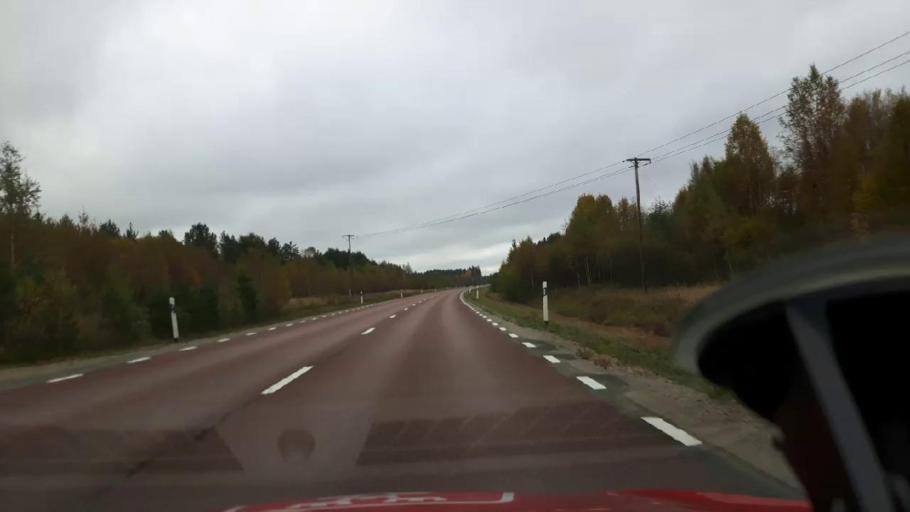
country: SE
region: Jaemtland
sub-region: Harjedalens Kommun
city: Sveg
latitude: 62.2565
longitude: 14.8196
